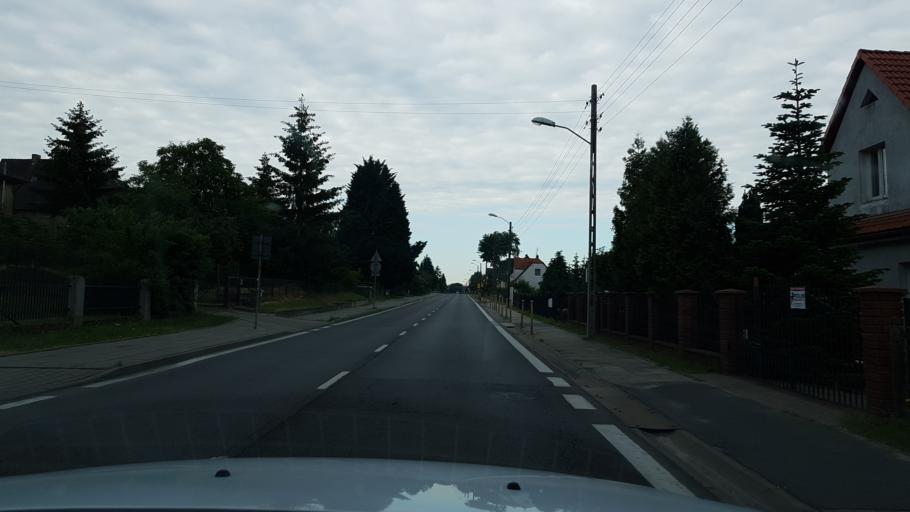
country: PL
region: West Pomeranian Voivodeship
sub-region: Szczecin
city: Szczecin
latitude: 53.3475
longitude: 14.5659
